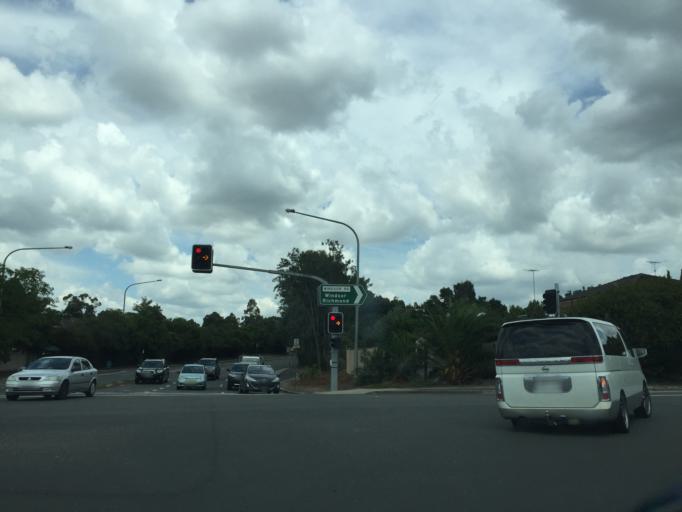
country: AU
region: New South Wales
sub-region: The Hills Shire
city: Beaumont Hills
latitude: -33.7083
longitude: 150.9414
